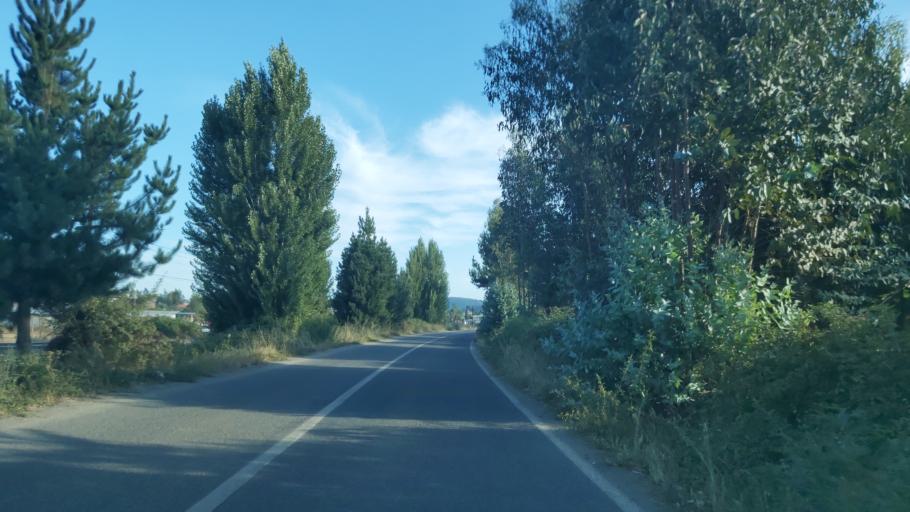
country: CL
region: Biobio
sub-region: Provincia de Biobio
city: La Laja
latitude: -37.1534
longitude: -72.9175
